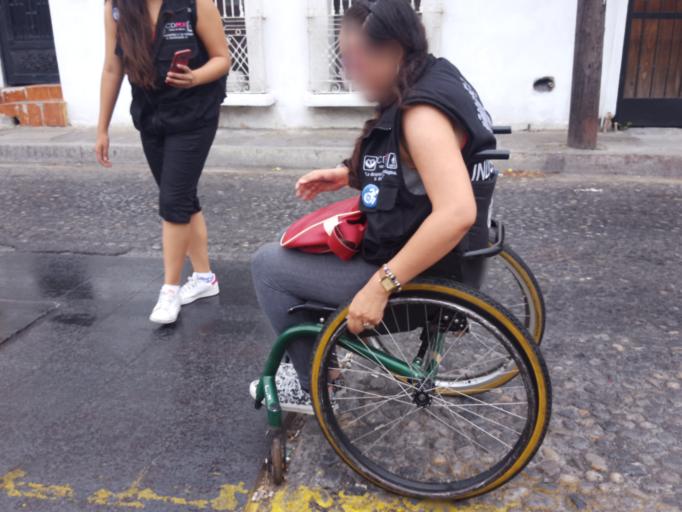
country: MX
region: Nuevo Leon
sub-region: Monterrey
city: Monterrey
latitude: 25.6703
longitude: -100.3054
